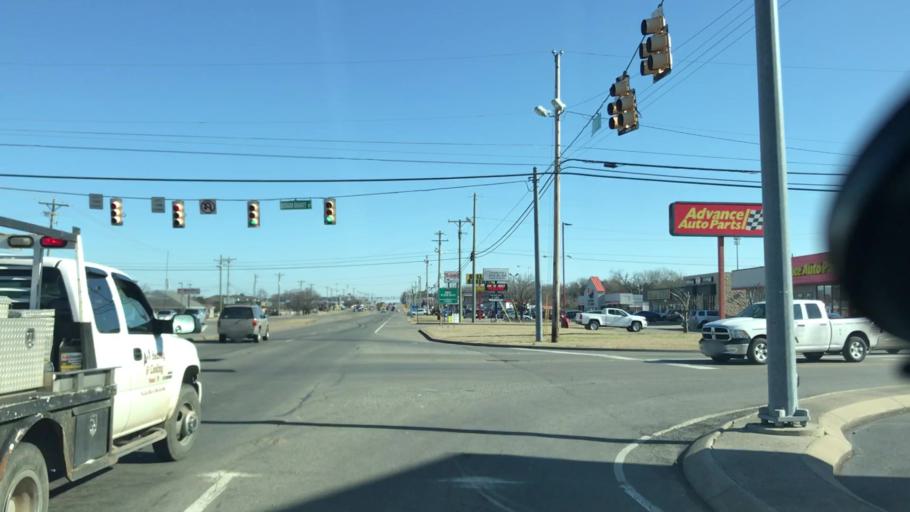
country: US
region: Tennessee
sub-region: Rutherford County
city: La Vergne
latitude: 36.0205
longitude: -86.5785
